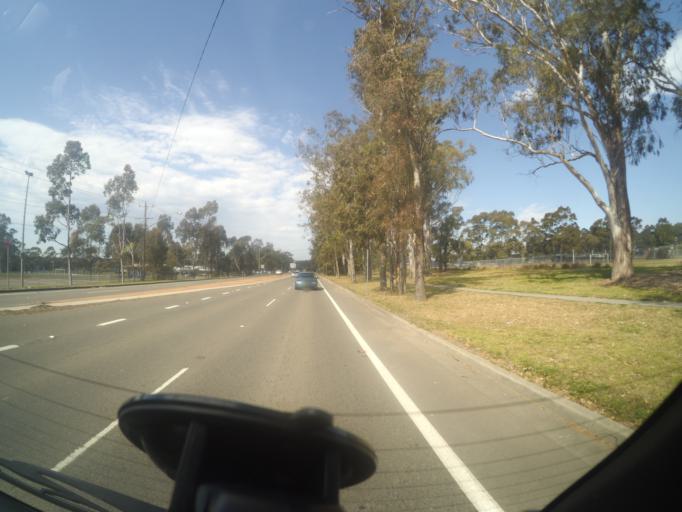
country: AU
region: New South Wales
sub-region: Bankstown
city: Milperra
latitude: -33.9538
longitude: 150.9538
